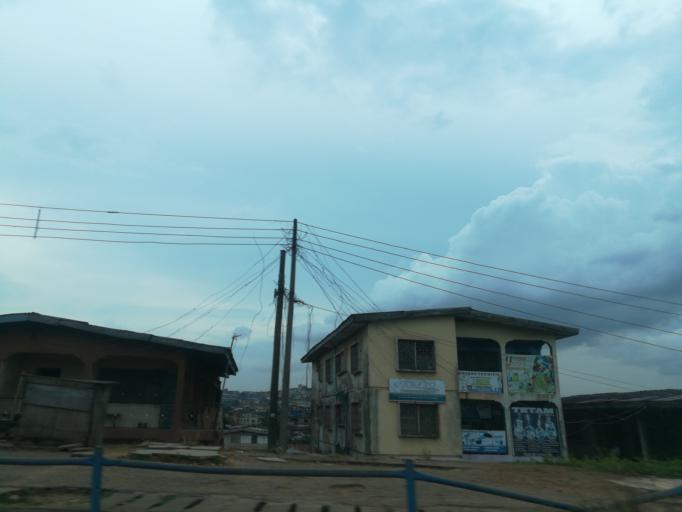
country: NG
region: Oyo
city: Ibadan
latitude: 7.4268
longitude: 3.8887
